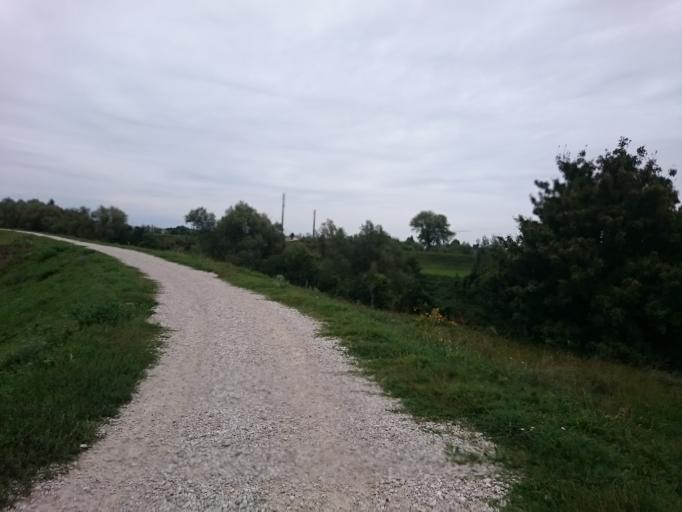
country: IT
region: Veneto
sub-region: Provincia di Vicenza
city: Quinto Vicentino
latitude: 45.5667
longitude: 11.6279
